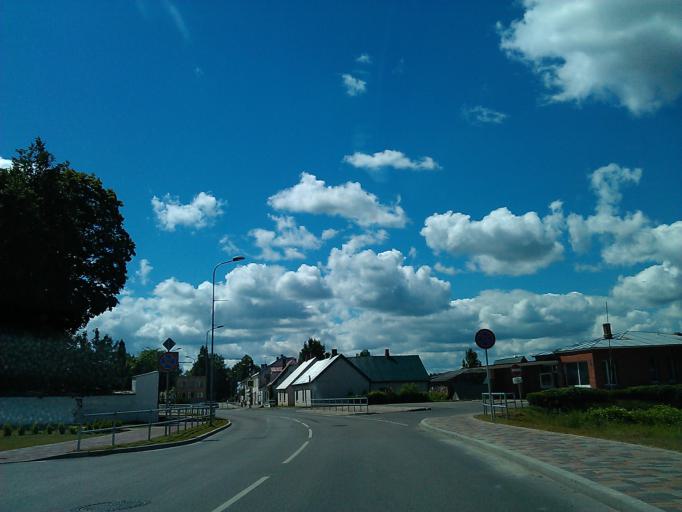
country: LV
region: Vilanu
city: Vilani
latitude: 56.5532
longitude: 26.9224
